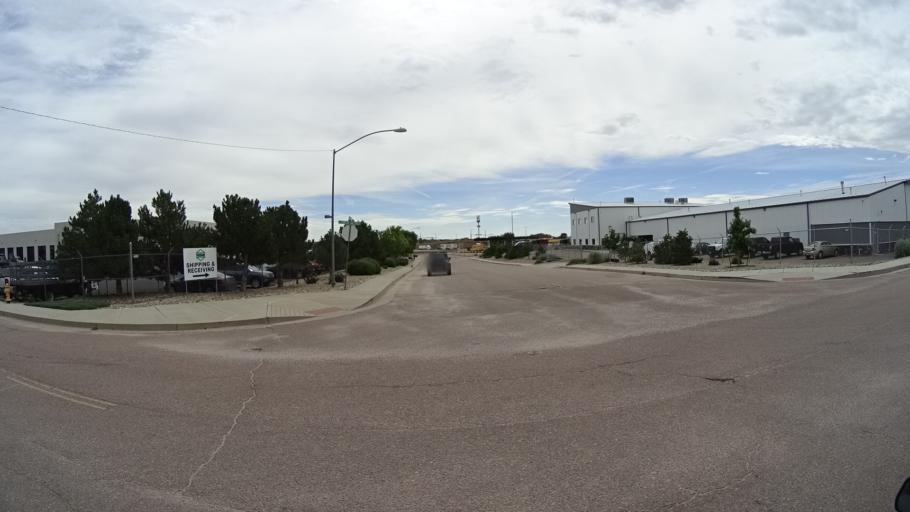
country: US
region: Colorado
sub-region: El Paso County
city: Fountain
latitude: 38.6732
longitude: -104.7150
